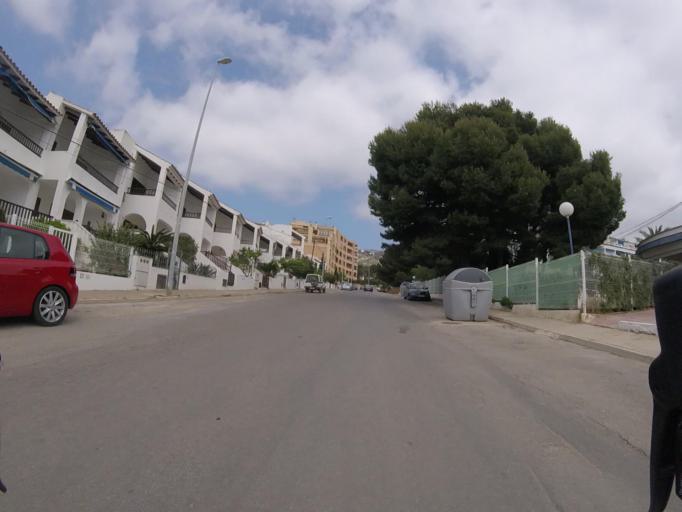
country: ES
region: Valencia
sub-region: Provincia de Castello
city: Alcoceber
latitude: 40.2554
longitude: 0.2890
